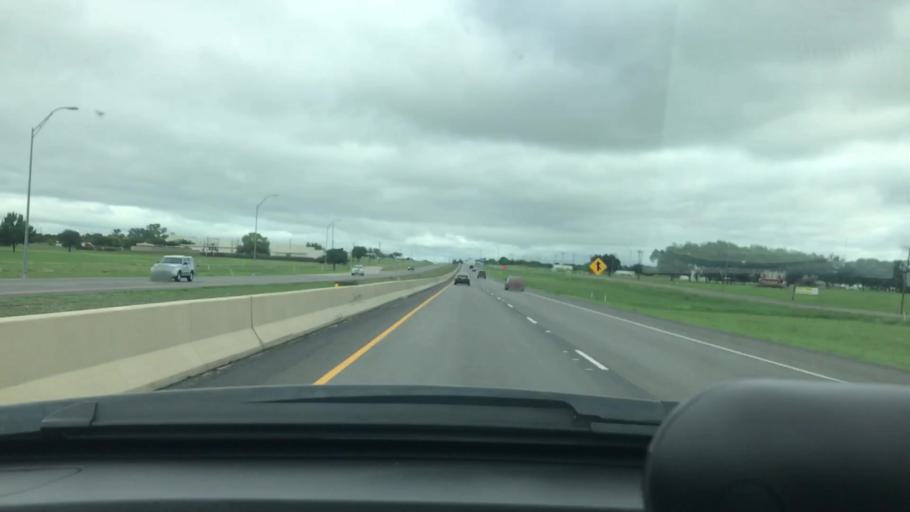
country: US
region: Texas
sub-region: Grayson County
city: Sherman
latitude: 33.5807
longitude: -96.6030
